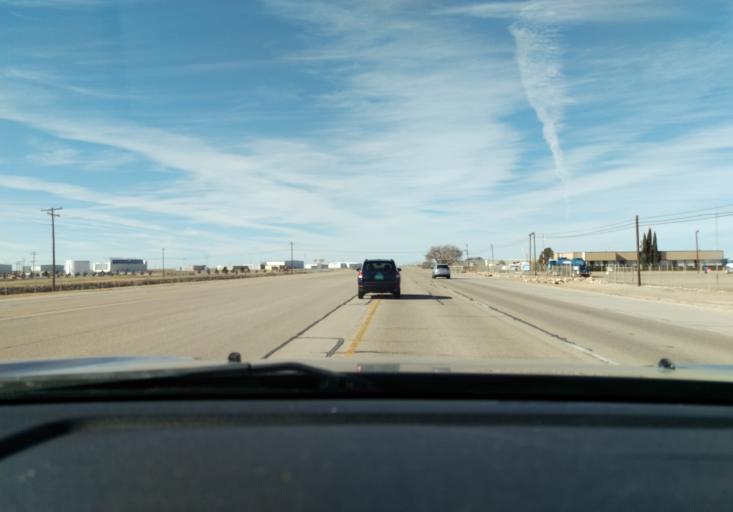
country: US
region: New Mexico
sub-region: Lea County
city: Hobbs
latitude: 32.6968
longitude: -103.2111
